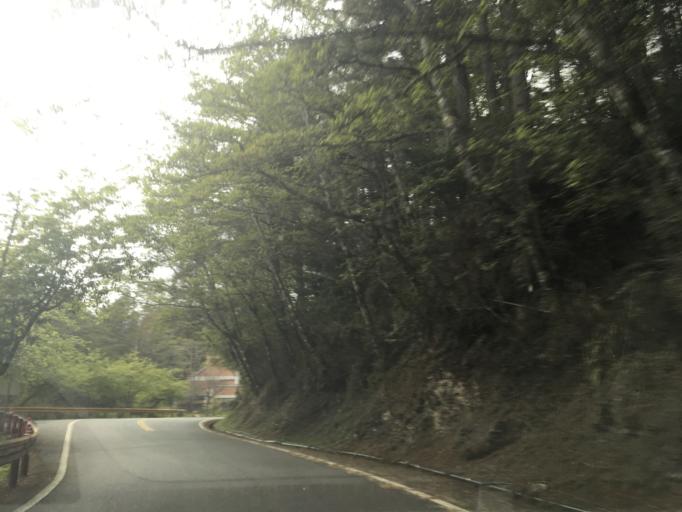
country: TW
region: Taiwan
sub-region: Hualien
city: Hualian
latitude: 24.1863
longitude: 121.3403
